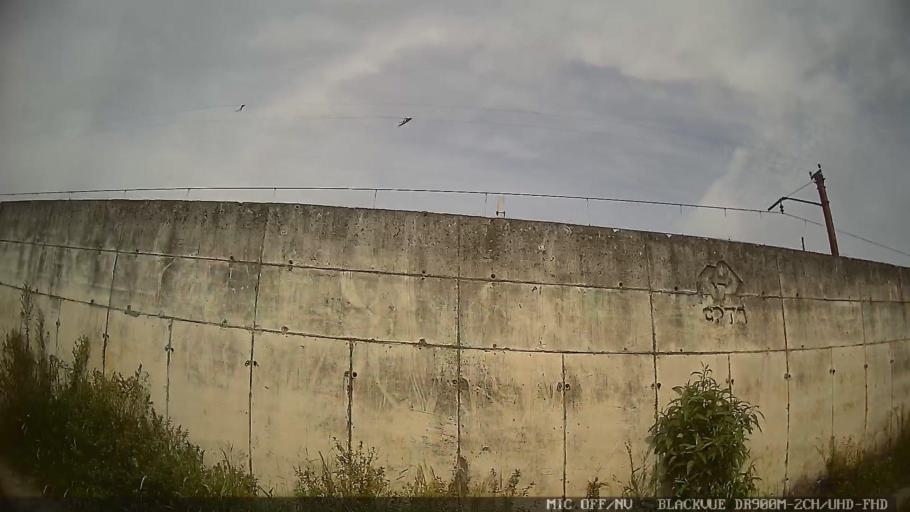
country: BR
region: Sao Paulo
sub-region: Itaquaquecetuba
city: Itaquaquecetuba
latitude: -23.4967
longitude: -46.3385
